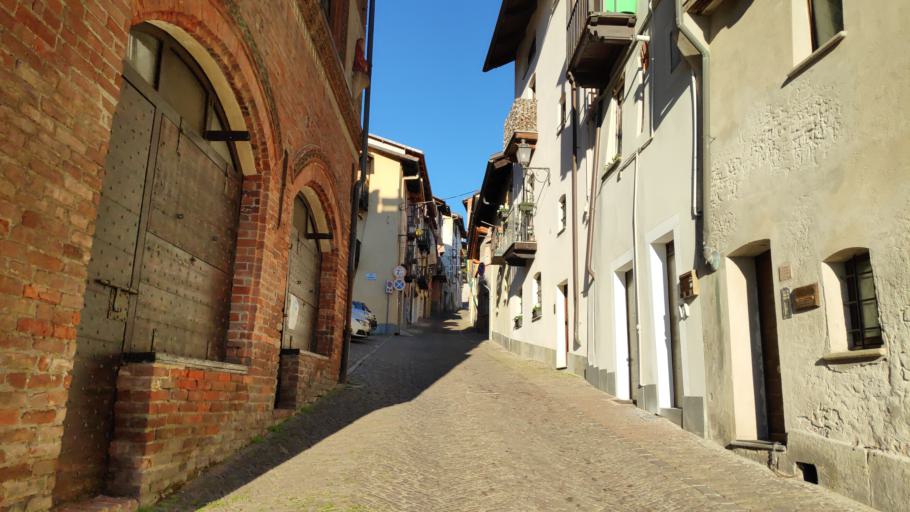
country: IT
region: Piedmont
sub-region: Provincia di Torino
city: Pinerolo
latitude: 44.8864
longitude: 7.3278
